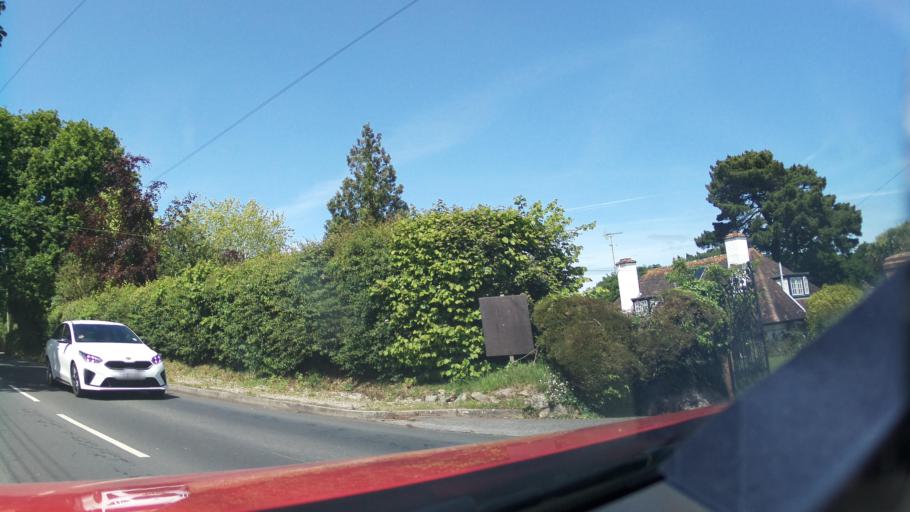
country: GB
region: England
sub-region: Devon
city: Budleigh Salterton
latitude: 50.6326
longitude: -3.3437
